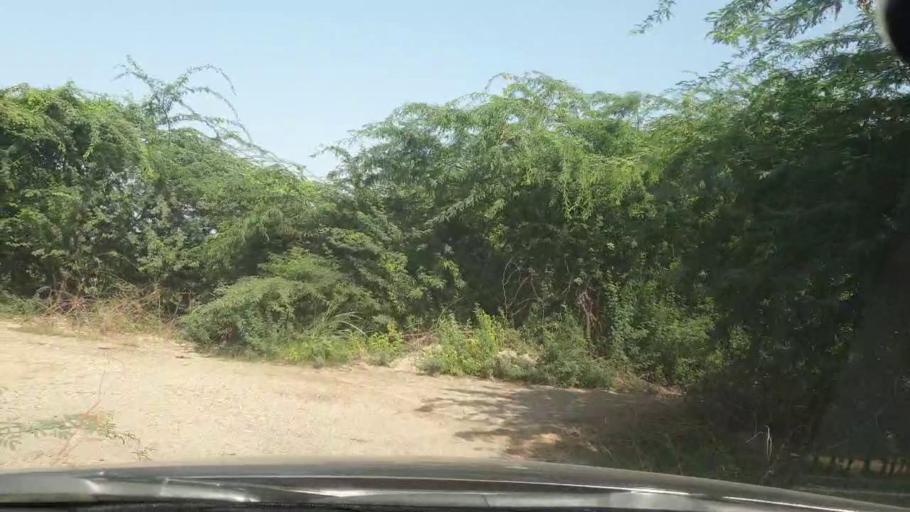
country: PK
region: Sindh
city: Naukot
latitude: 24.7986
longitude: 69.2637
